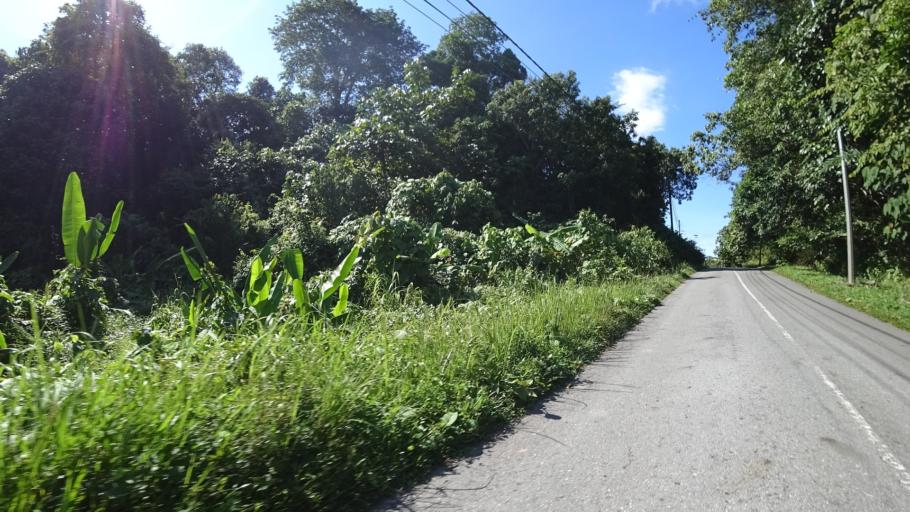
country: BN
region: Tutong
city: Tutong
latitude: 4.7490
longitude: 114.7838
